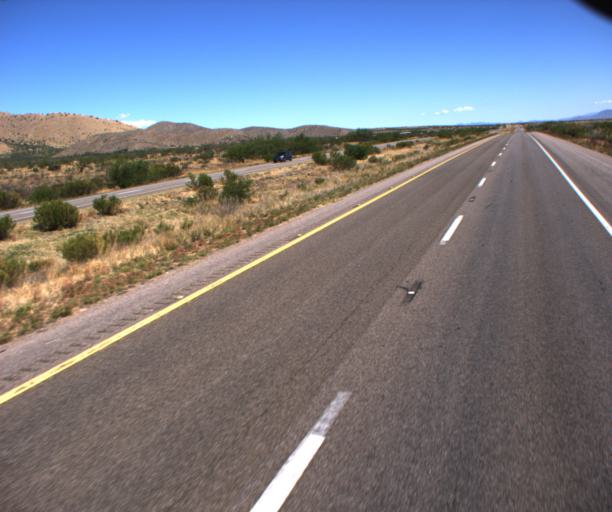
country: US
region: Arizona
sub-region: Cochise County
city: Whetstone
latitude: 31.8241
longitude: -110.3457
